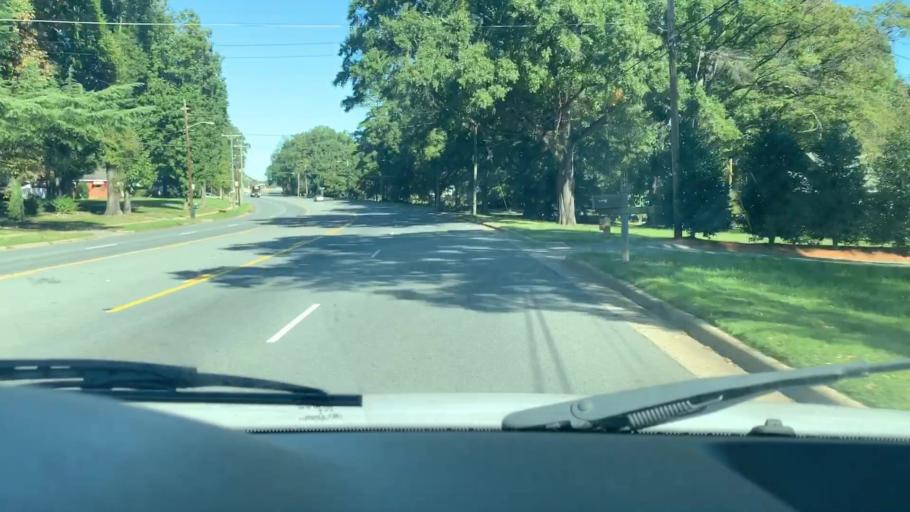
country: US
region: North Carolina
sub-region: Mecklenburg County
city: Charlotte
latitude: 35.2847
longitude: -80.7935
